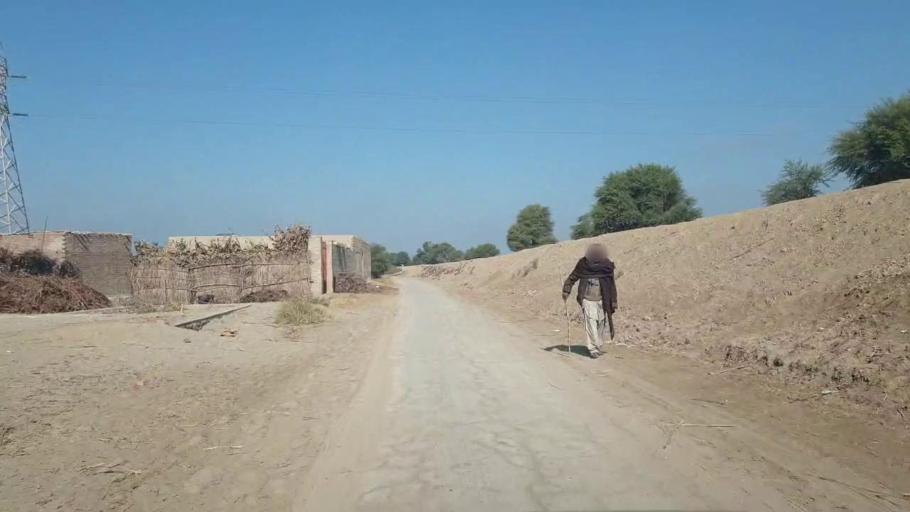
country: PK
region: Sindh
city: Shahdadpur
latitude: 25.8811
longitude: 68.5459
